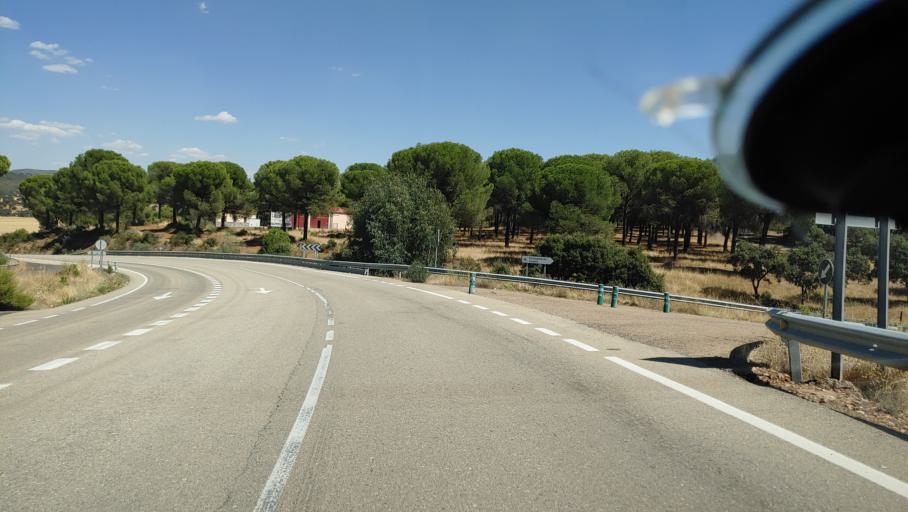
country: ES
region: Castille-La Mancha
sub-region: Provincia de Ciudad Real
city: Saceruela
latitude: 39.0097
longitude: -4.5013
